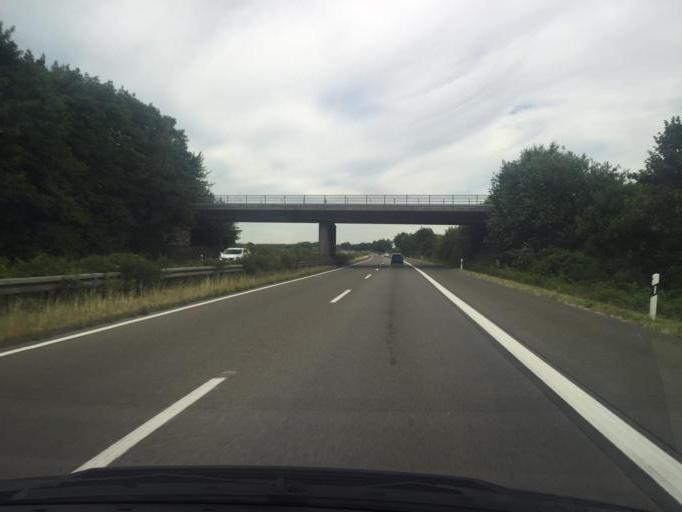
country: DE
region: North Rhine-Westphalia
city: Rheinberg
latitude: 51.5412
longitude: 6.5683
